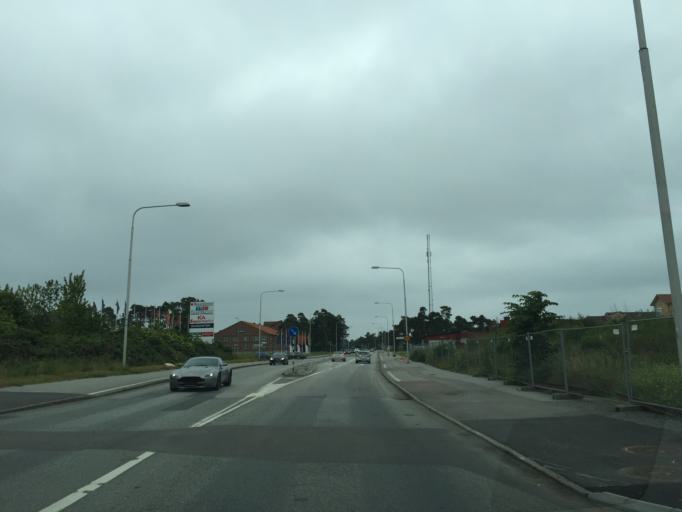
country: SE
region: Skane
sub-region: Ystads Kommun
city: Ystad
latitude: 55.4353
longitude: 13.8380
